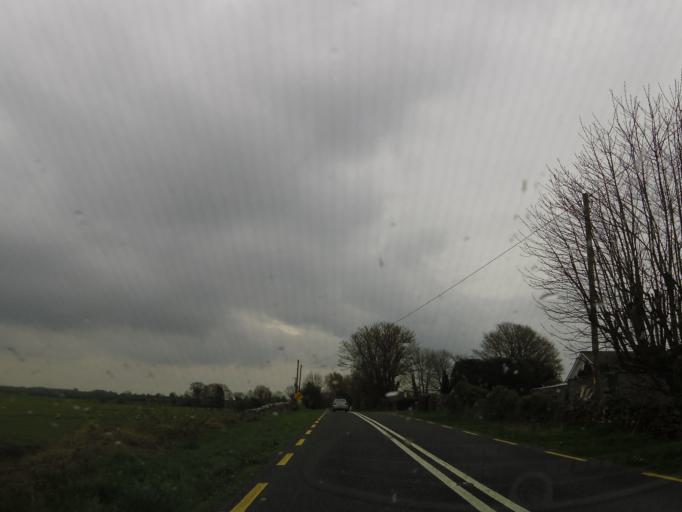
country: IE
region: Connaught
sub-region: Maigh Eo
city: Claremorris
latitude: 53.6536
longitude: -8.9489
